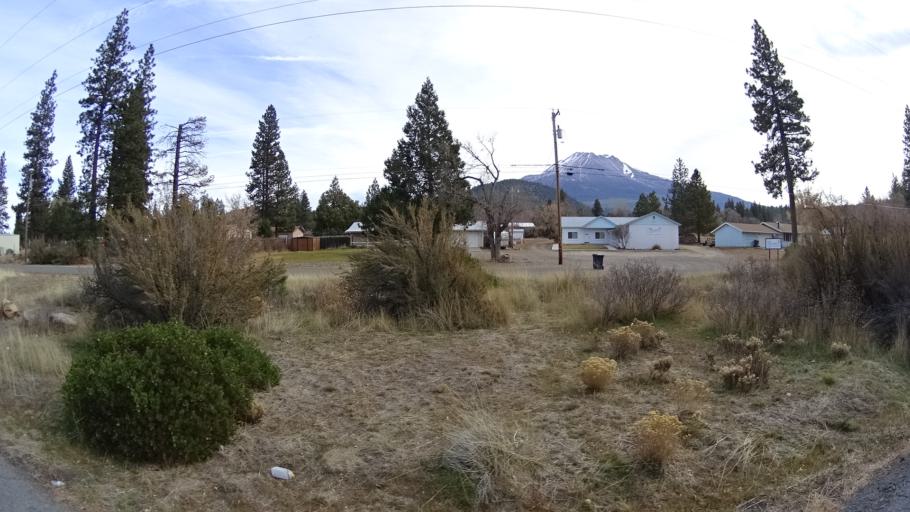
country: US
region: California
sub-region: Siskiyou County
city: Weed
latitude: 41.4495
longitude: -122.3621
